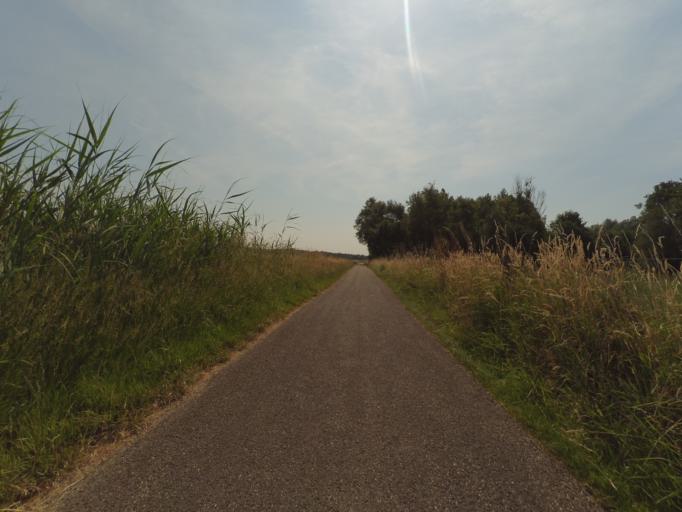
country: NL
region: North Brabant
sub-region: Gemeente Breda
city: Breda
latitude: 51.5177
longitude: 4.7865
